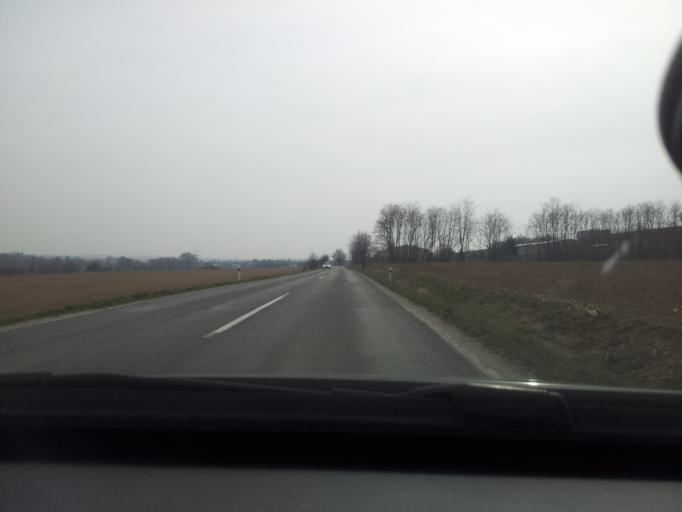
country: SK
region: Trnavsky
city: Hlohovec
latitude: 48.3797
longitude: 17.8744
